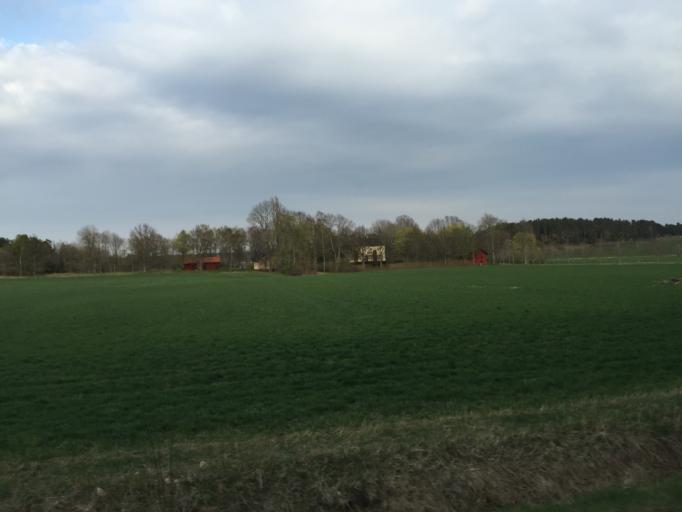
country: SE
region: Soedermanland
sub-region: Trosa Kommun
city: Vagnharad
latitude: 59.0366
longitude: 17.6002
